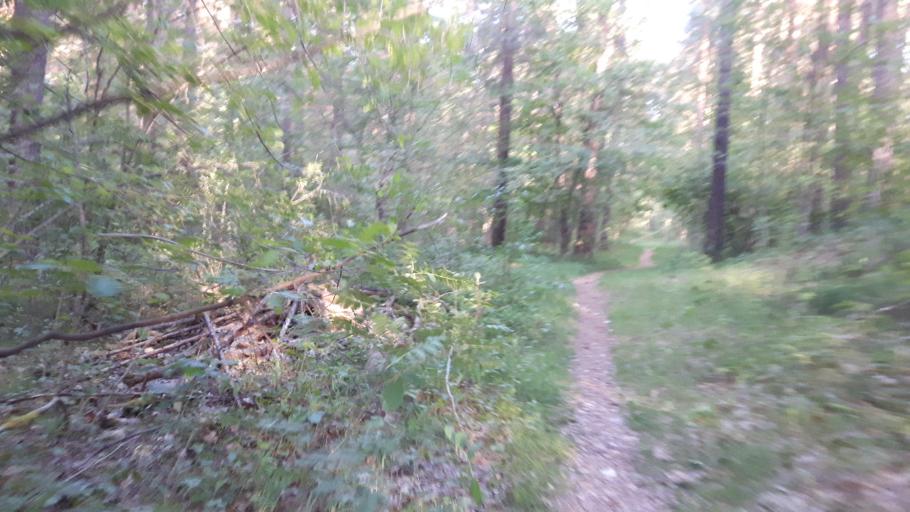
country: LV
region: Riga
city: Jaunciems
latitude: 57.0109
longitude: 24.1364
